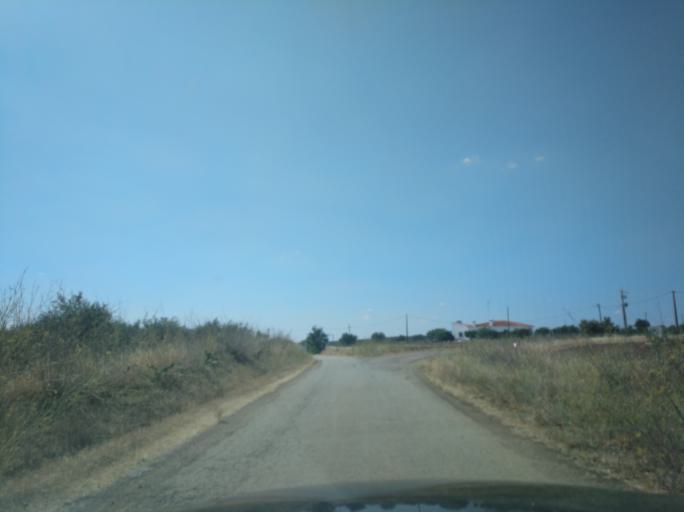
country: PT
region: Portalegre
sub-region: Campo Maior
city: Campo Maior
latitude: 39.0244
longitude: -7.0901
